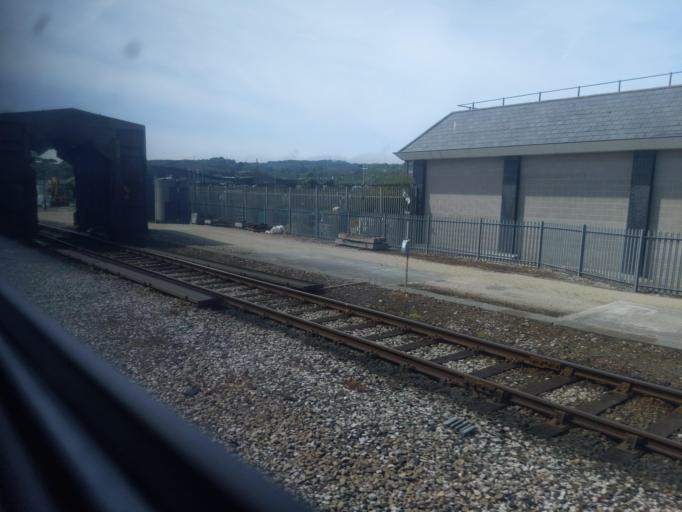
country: GB
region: England
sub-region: Cornwall
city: Penzance
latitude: 50.1275
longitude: -5.5143
